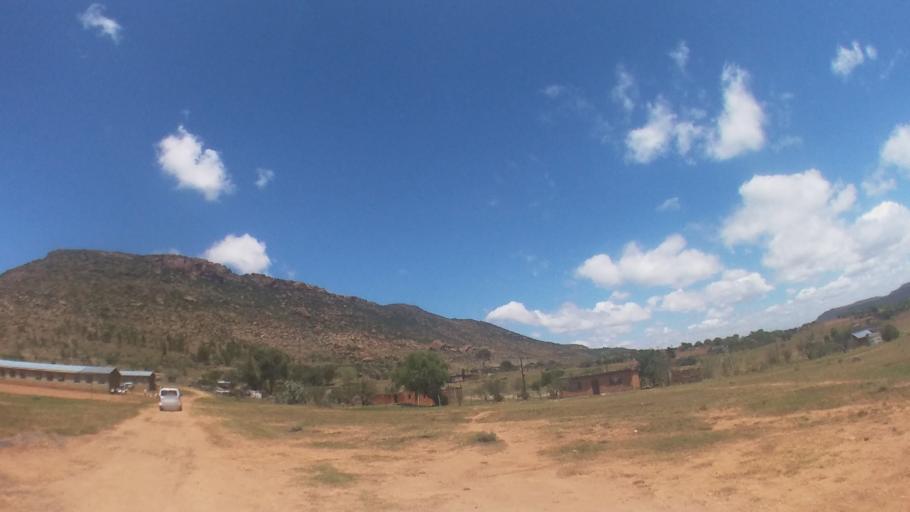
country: LS
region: Maseru
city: Maseru
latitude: -29.4399
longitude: 27.4130
